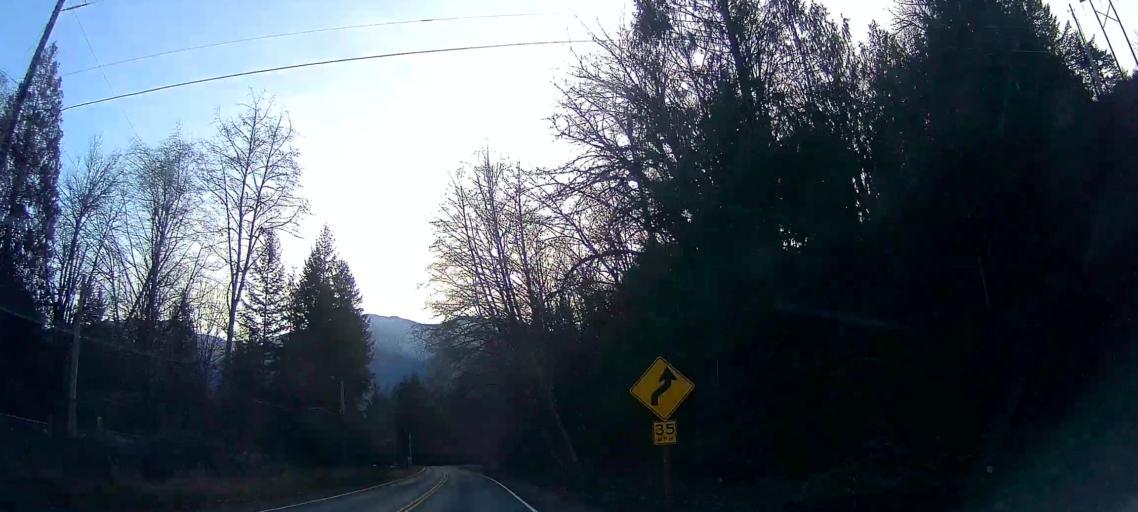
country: US
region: Washington
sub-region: Skagit County
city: Sedro-Woolley
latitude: 48.5372
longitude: -121.8848
